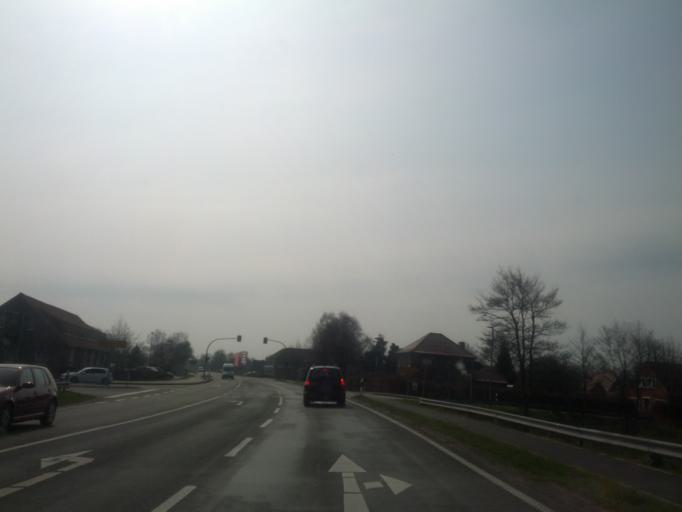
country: DE
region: Lower Saxony
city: Osteel
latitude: 53.5480
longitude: 7.2552
